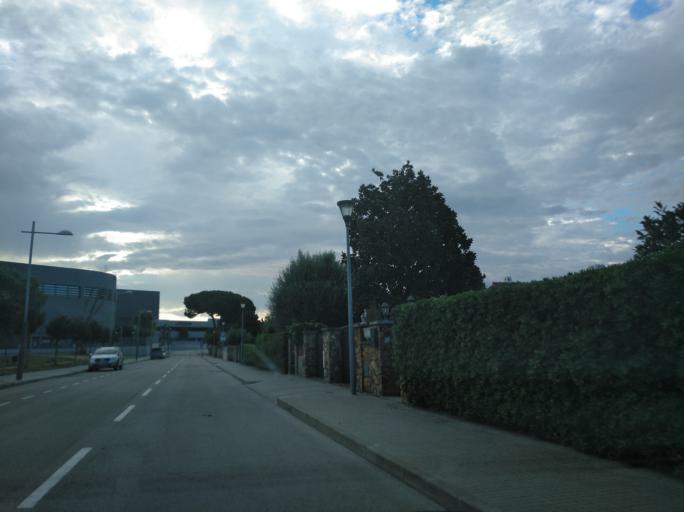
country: ES
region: Catalonia
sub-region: Provincia de Barcelona
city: Tordera
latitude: 41.6954
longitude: 2.7270
